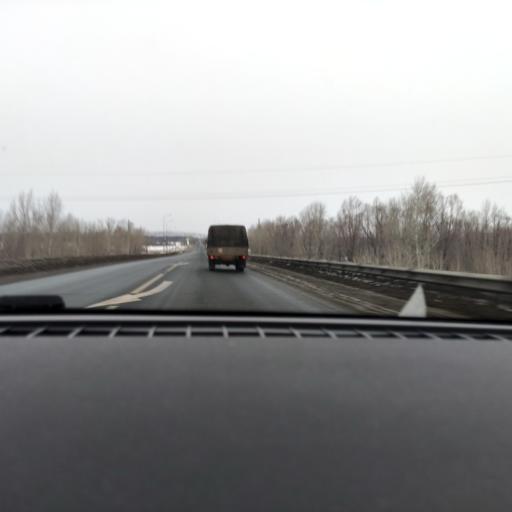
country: RU
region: Samara
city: Kinel'
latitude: 53.1892
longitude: 50.5151
